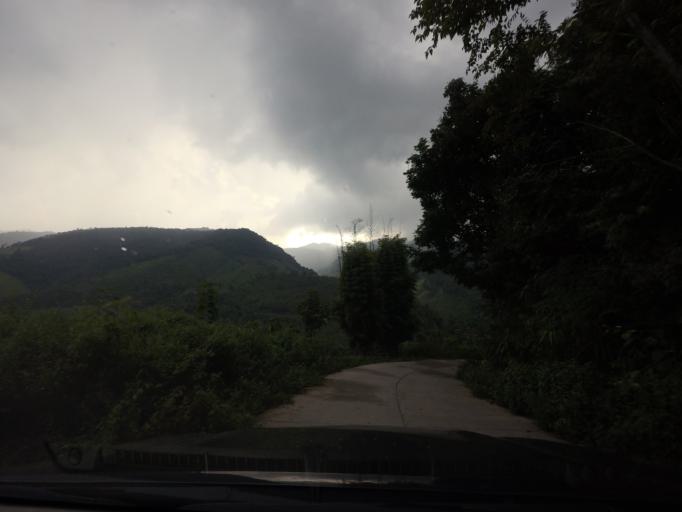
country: TH
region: Nan
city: Bo Kluea
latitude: 19.3507
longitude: 101.1625
